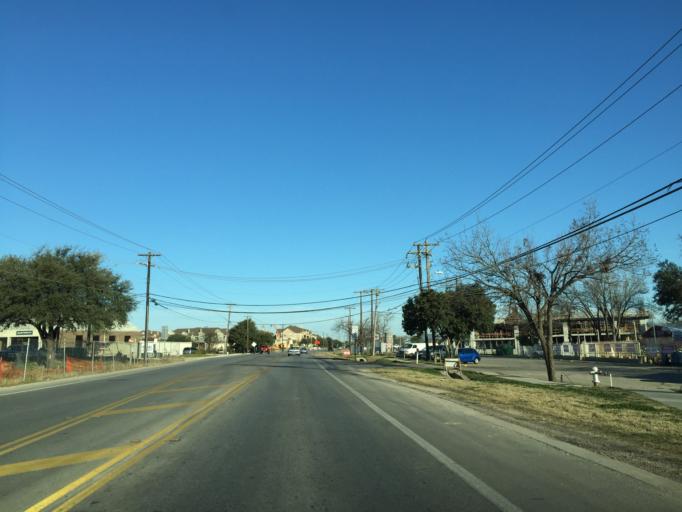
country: US
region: Texas
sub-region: Williamson County
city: Jollyville
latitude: 30.4362
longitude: -97.7707
